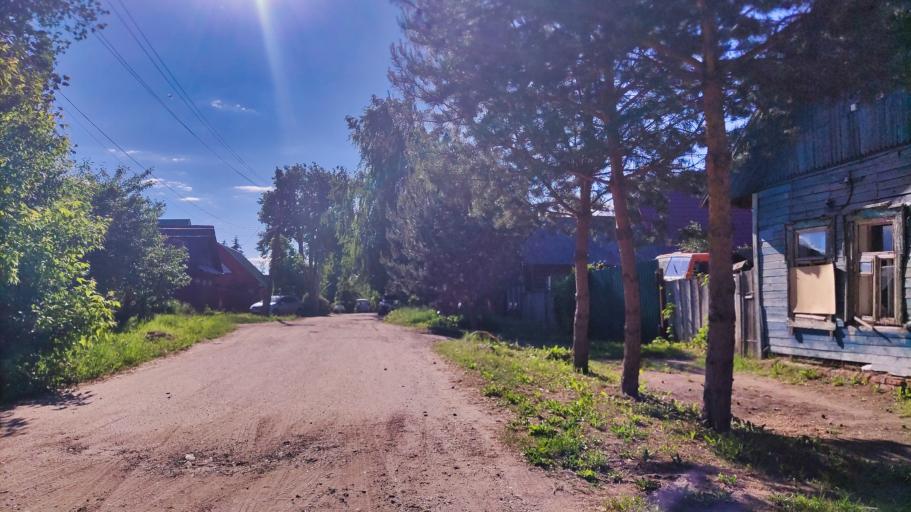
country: RU
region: Tverskaya
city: Rzhev
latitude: 56.2532
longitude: 34.3396
